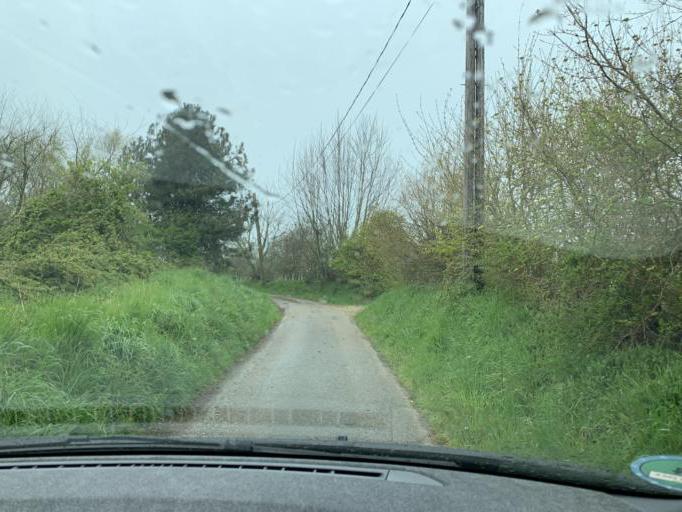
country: FR
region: Haute-Normandie
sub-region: Departement de la Seine-Maritime
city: Les Loges
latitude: 49.7292
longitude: 0.2792
